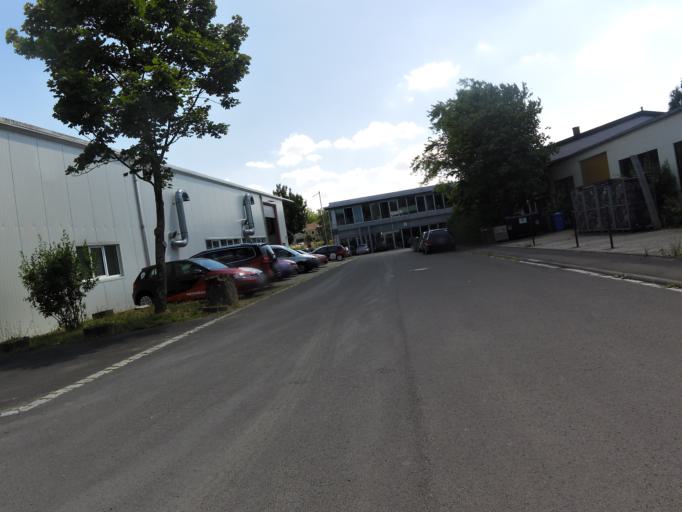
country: DE
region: Bavaria
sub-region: Regierungsbezirk Unterfranken
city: Gadheim
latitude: 49.8311
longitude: 9.9008
